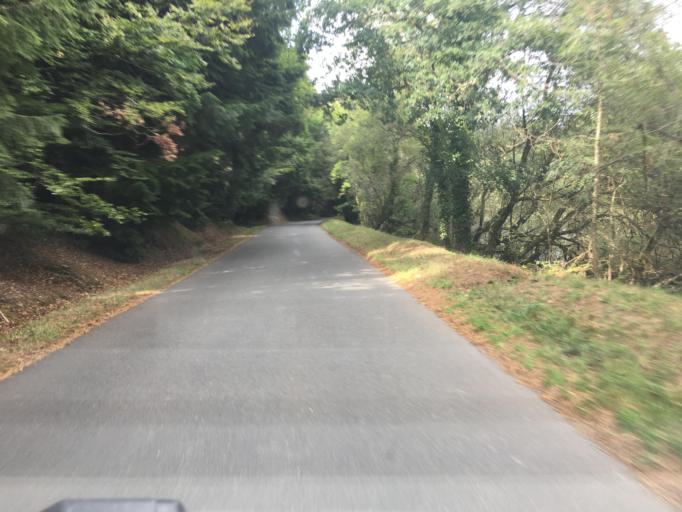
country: FR
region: Brittany
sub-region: Departement des Cotes-d'Armor
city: Gouarec
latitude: 48.2072
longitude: -3.1159
